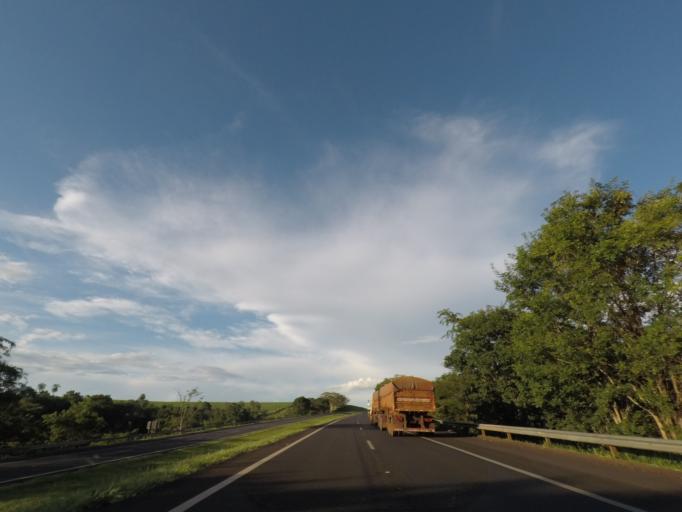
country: BR
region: Sao Paulo
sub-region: Ituverava
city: Ituverava
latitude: -20.2549
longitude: -47.7998
